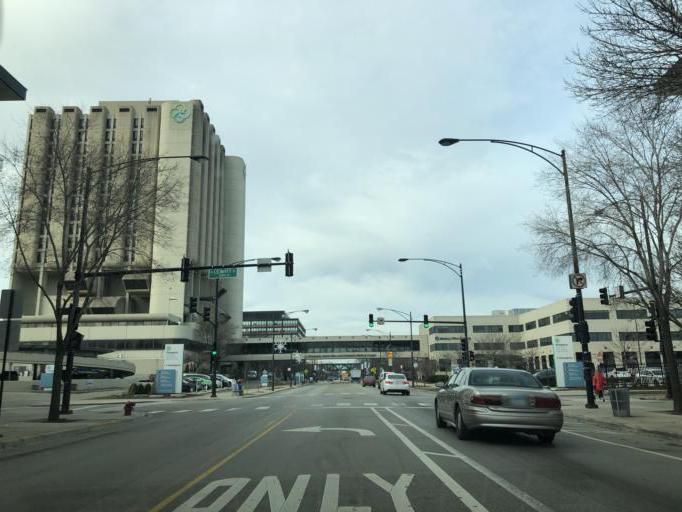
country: US
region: Illinois
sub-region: Cook County
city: Chicago
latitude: 41.9031
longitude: -87.6818
